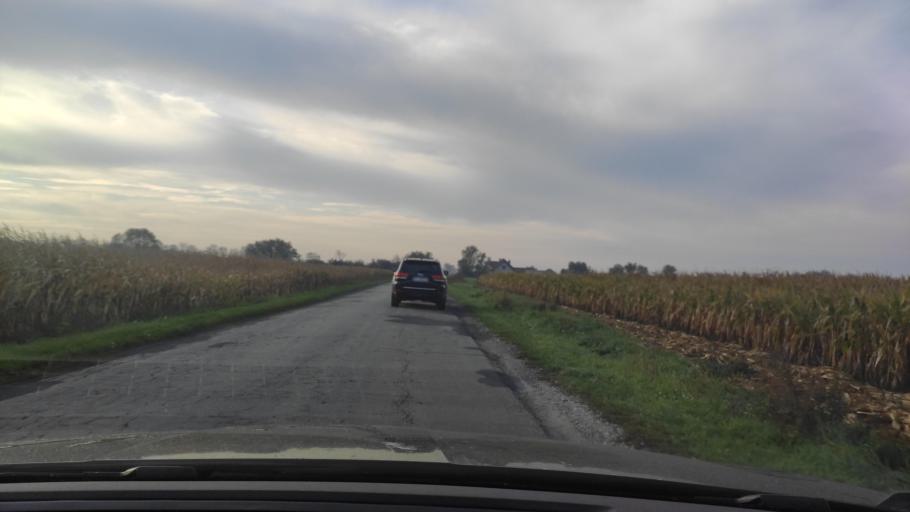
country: PL
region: Greater Poland Voivodeship
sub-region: Powiat poznanski
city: Kleszczewo
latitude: 52.3736
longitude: 17.1669
